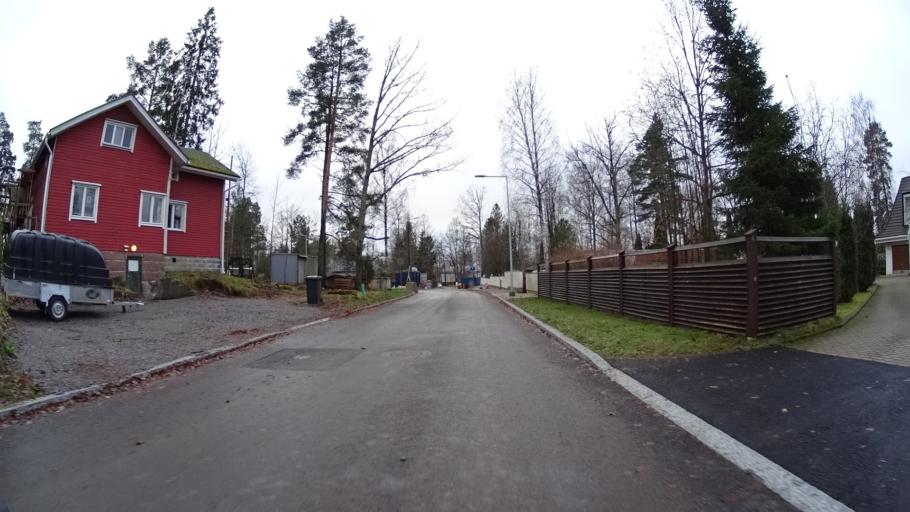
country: FI
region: Uusimaa
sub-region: Helsinki
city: Kilo
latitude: 60.2473
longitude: 24.7548
